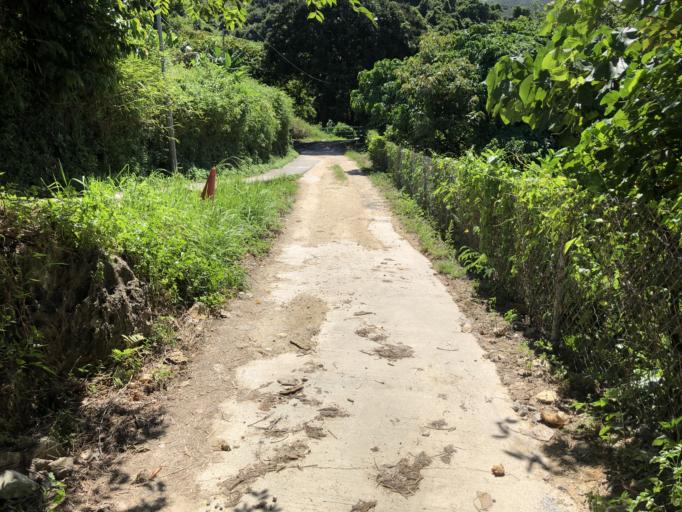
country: HK
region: Tuen Mun
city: Tuen Mun
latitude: 22.2909
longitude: 113.9786
